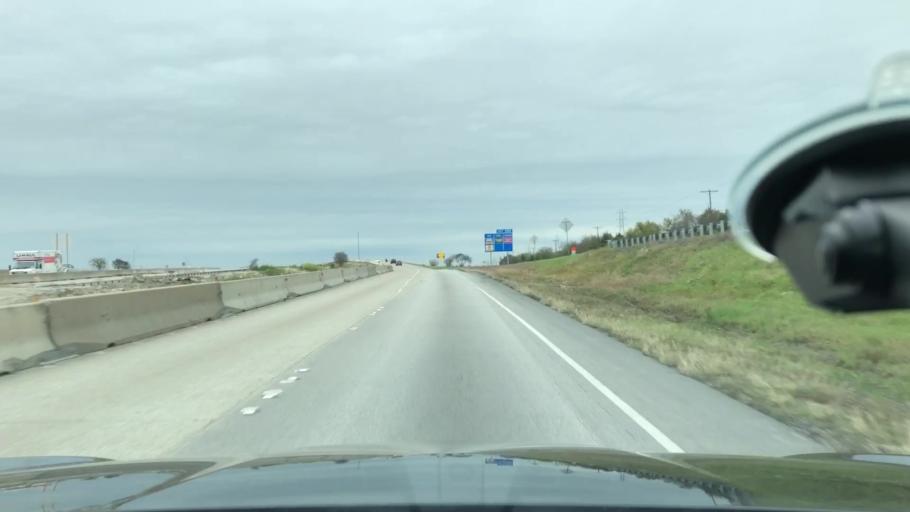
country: US
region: Texas
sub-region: Ellis County
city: Waxahachie
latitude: 32.3585
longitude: -96.8548
